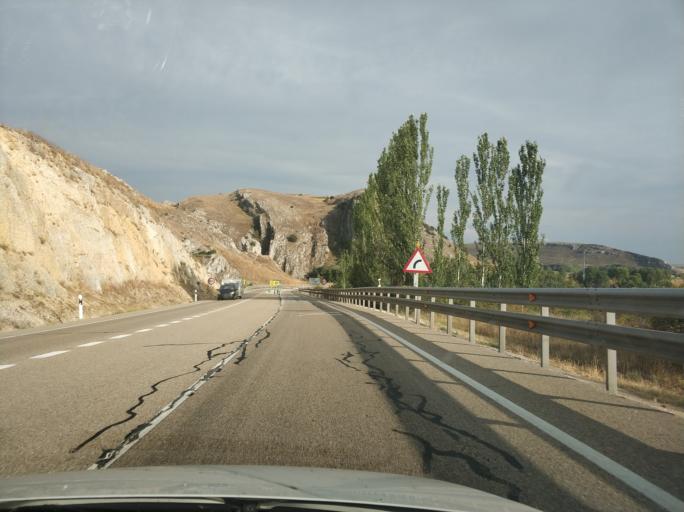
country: ES
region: Castille and Leon
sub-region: Provincia de Burgos
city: Quintanaortuno
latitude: 42.5079
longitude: -3.7072
